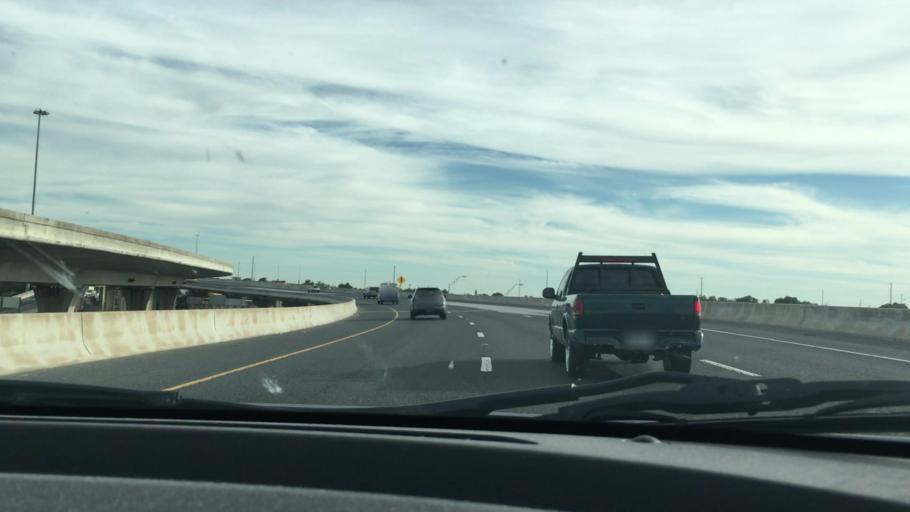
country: US
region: Texas
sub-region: Bexar County
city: San Antonio
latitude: 29.4445
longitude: -98.5151
